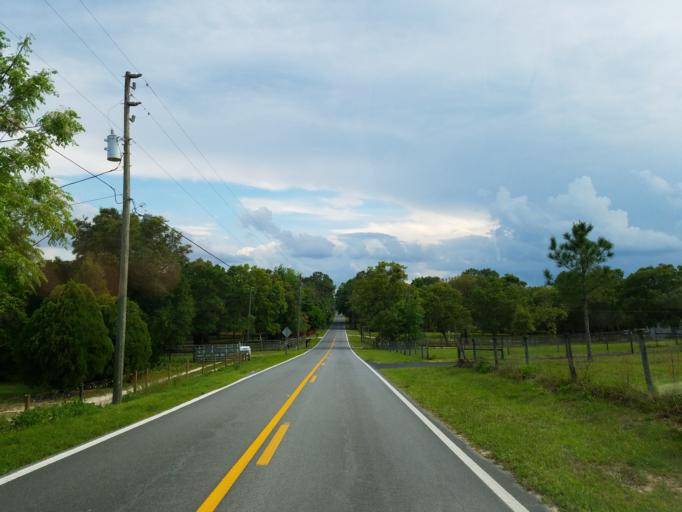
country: US
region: Florida
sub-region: Hernando County
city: Hill 'n Dale
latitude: 28.5344
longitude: -82.2759
